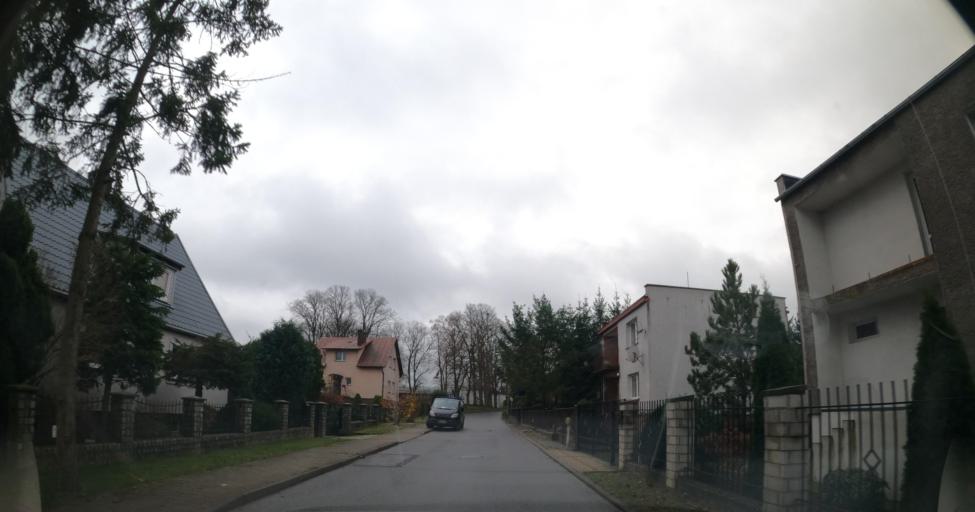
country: PL
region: West Pomeranian Voivodeship
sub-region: Powiat drawski
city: Drawsko Pomorskie
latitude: 53.5307
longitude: 15.8200
